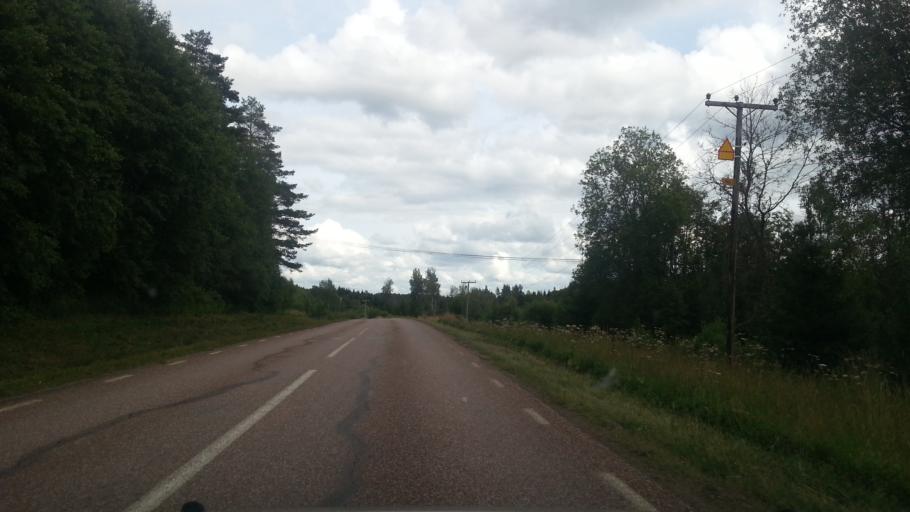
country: SE
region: Dalarna
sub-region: Borlange Kommun
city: Ornas
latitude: 60.3343
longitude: 15.5695
